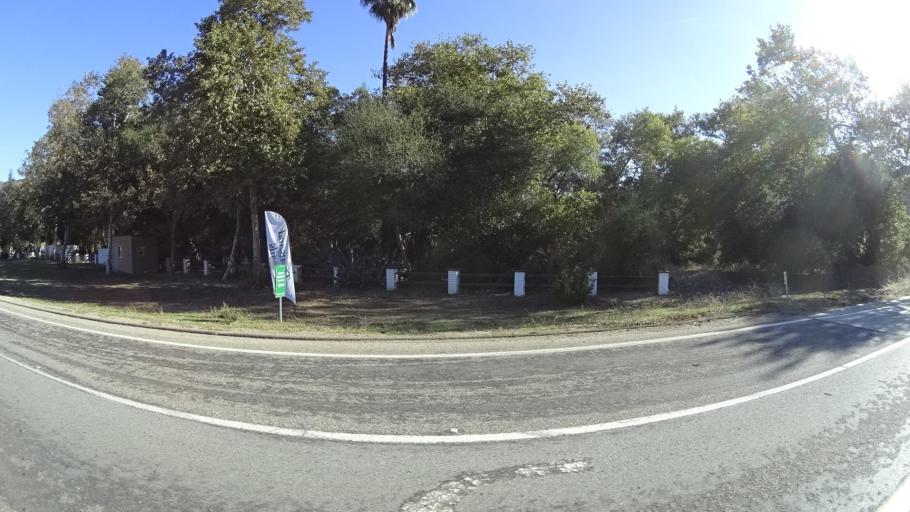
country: US
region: California
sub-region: San Diego County
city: Jamul
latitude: 32.6520
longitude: -116.8544
